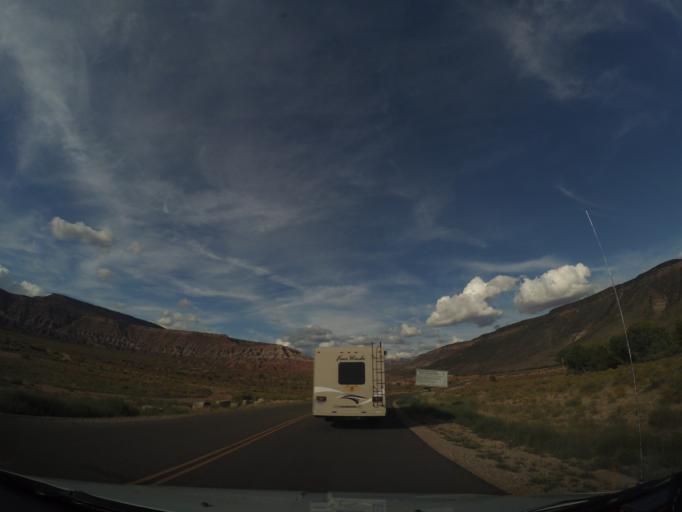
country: US
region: Utah
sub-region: Washington County
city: LaVerkin
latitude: 37.2109
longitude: -113.1757
